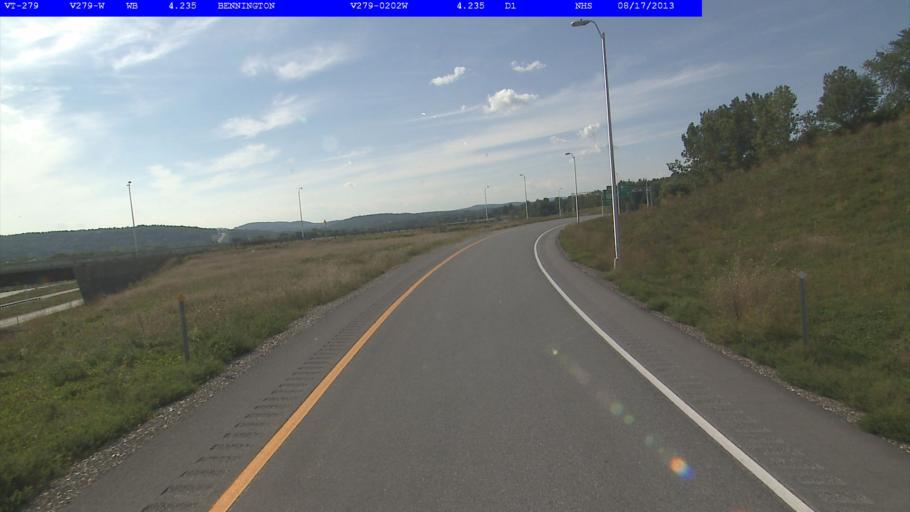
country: US
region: Vermont
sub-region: Bennington County
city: Bennington
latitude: 42.9025
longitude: -73.1985
